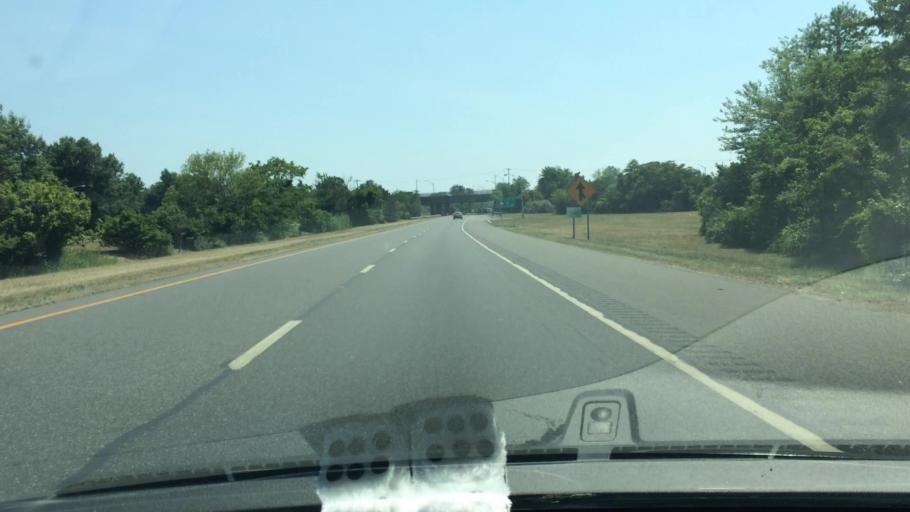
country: US
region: New Jersey
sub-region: Gloucester County
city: Beckett
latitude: 39.7809
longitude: -75.3375
